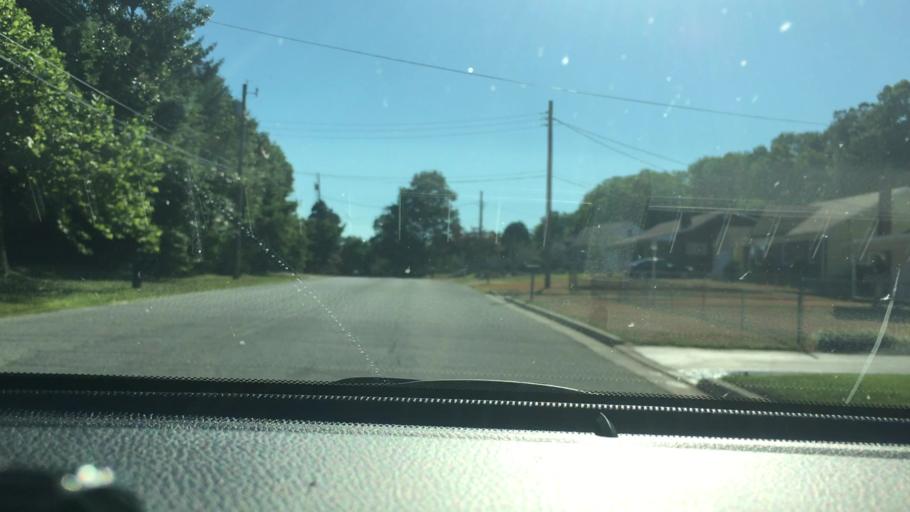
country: US
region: New Jersey
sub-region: Cumberland County
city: Millville
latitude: 39.3954
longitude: -75.0616
